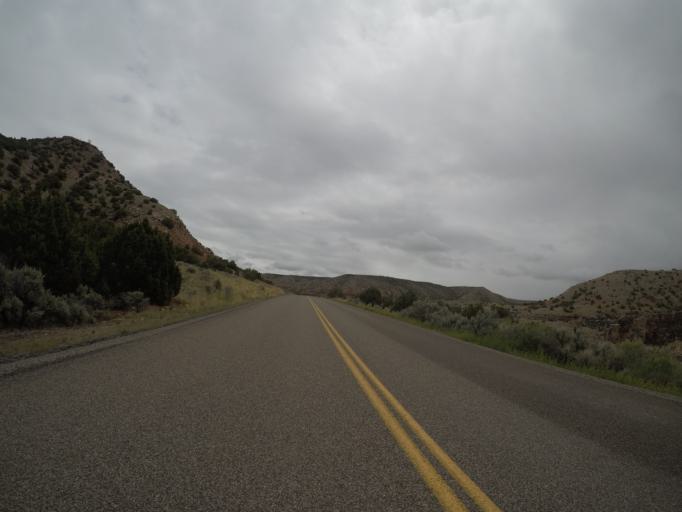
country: US
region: Wyoming
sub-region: Big Horn County
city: Lovell
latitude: 45.0991
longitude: -108.2171
